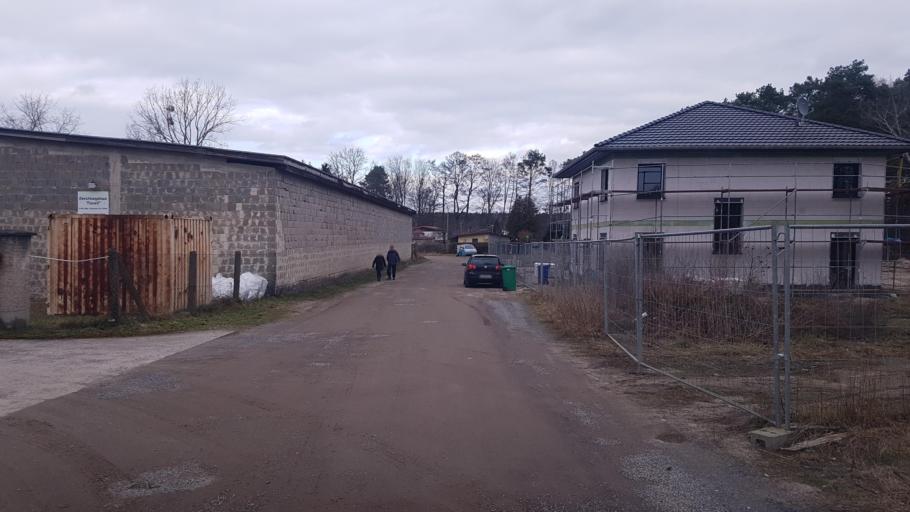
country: DE
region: Brandenburg
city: Halbe
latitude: 52.1109
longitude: 13.6913
